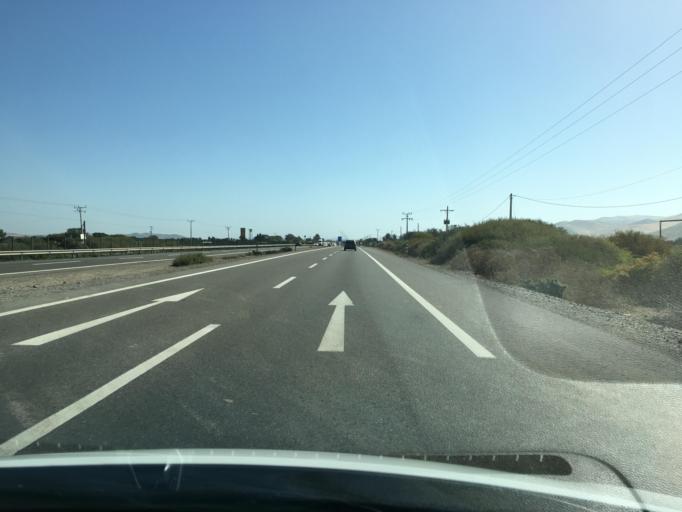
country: CL
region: Atacama
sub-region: Provincia de Copiapo
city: Copiapo
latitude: -27.3184
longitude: -70.5262
